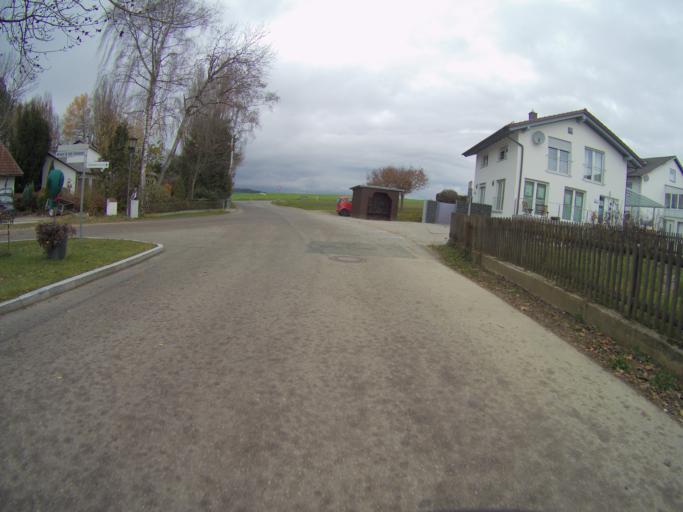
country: DE
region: Bavaria
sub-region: Upper Bavaria
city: Langenbach
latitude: 48.4126
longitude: 11.8328
